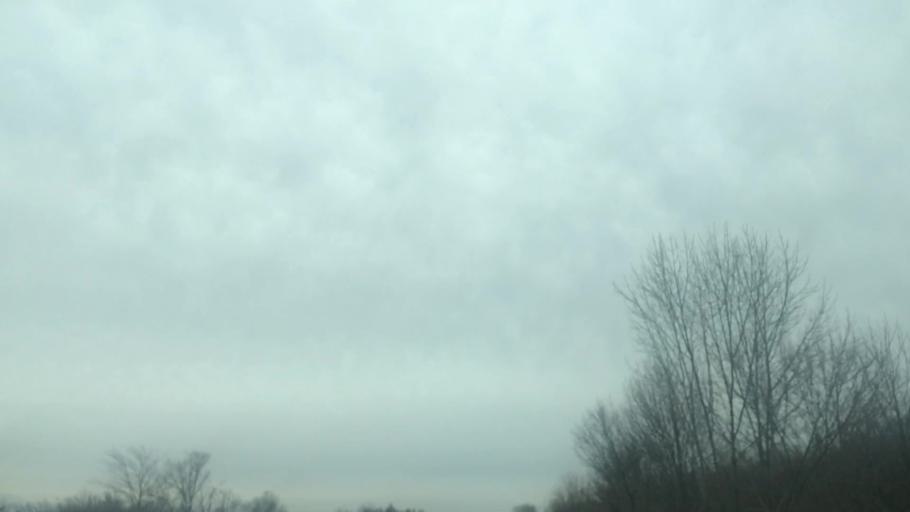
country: US
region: New York
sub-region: Rockland County
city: Chestnut Ridge
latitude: 41.0705
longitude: -74.0537
